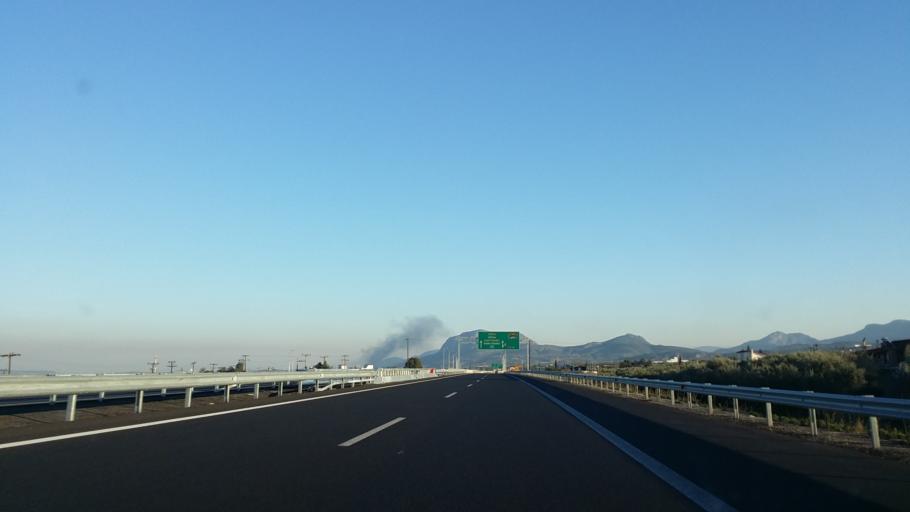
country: GR
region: Peloponnese
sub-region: Nomos Korinthias
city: Vokhaiko
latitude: 37.9337
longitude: 22.7787
